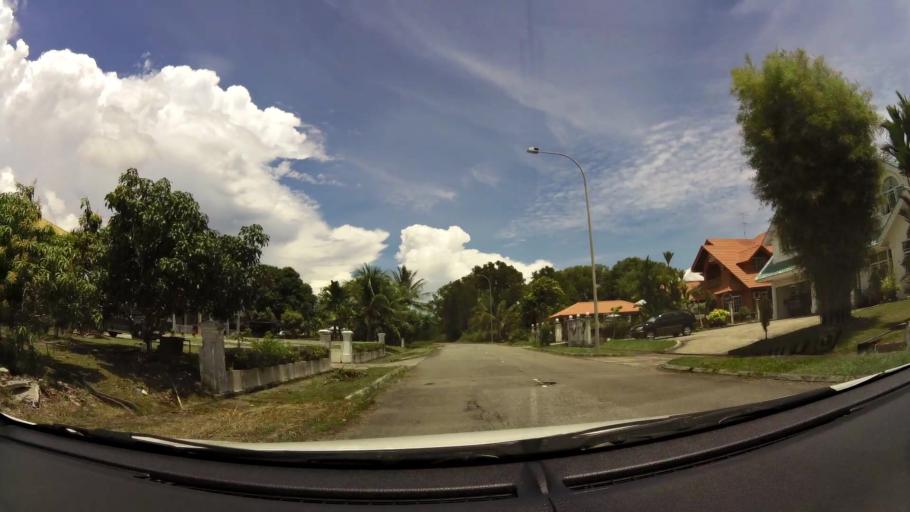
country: BN
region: Brunei and Muara
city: Bandar Seri Begawan
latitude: 4.9616
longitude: 114.9144
